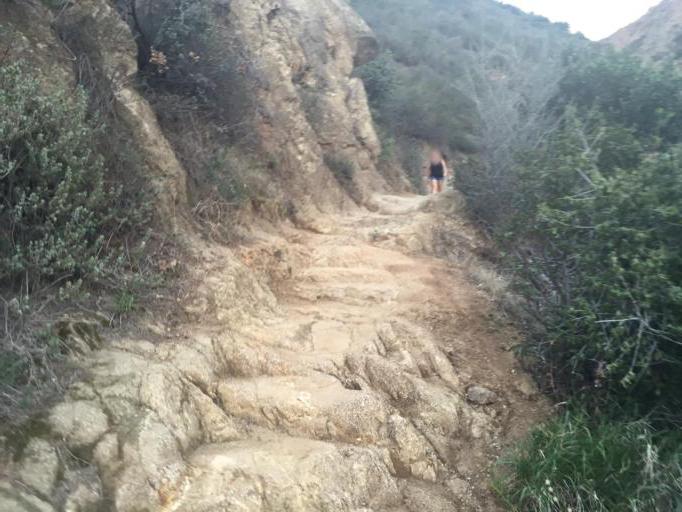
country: US
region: California
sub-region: Los Angeles County
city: Sierra Madre
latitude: 34.1757
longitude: -118.0456
